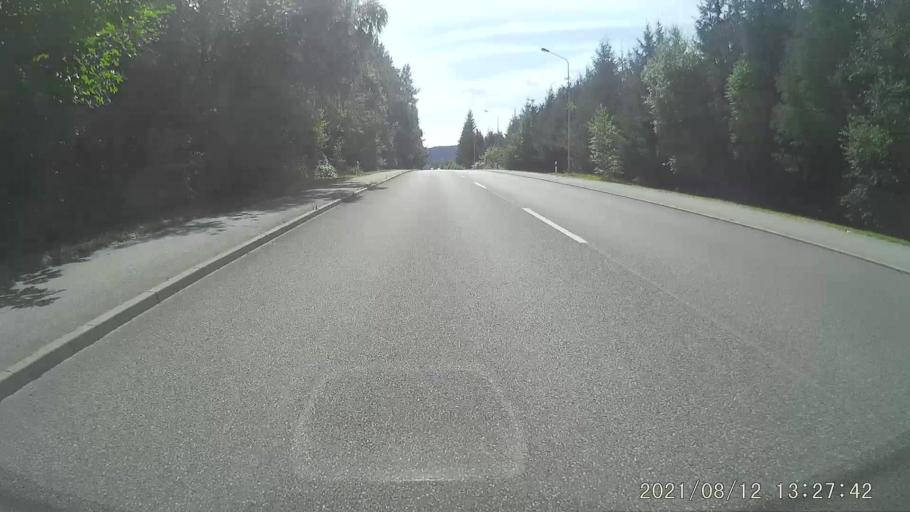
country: PL
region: Lower Silesian Voivodeship
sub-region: Powiat klodzki
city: Ladek-Zdroj
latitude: 50.3373
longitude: 16.8706
